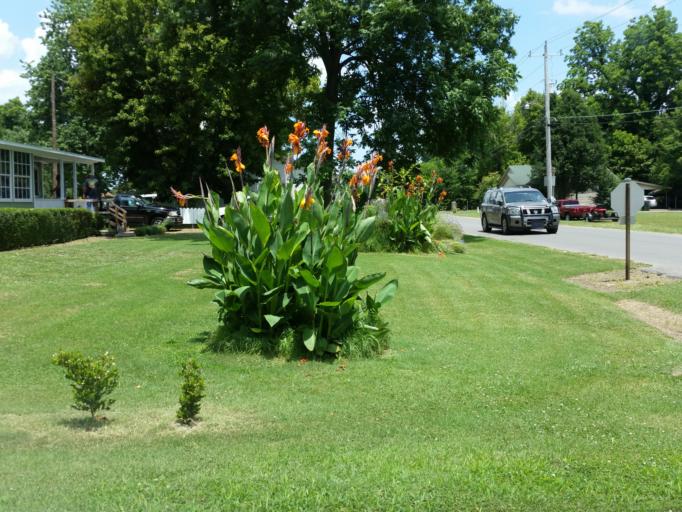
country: US
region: Tennessee
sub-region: Lake County
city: Tiptonville
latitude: 36.3750
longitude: -89.4840
